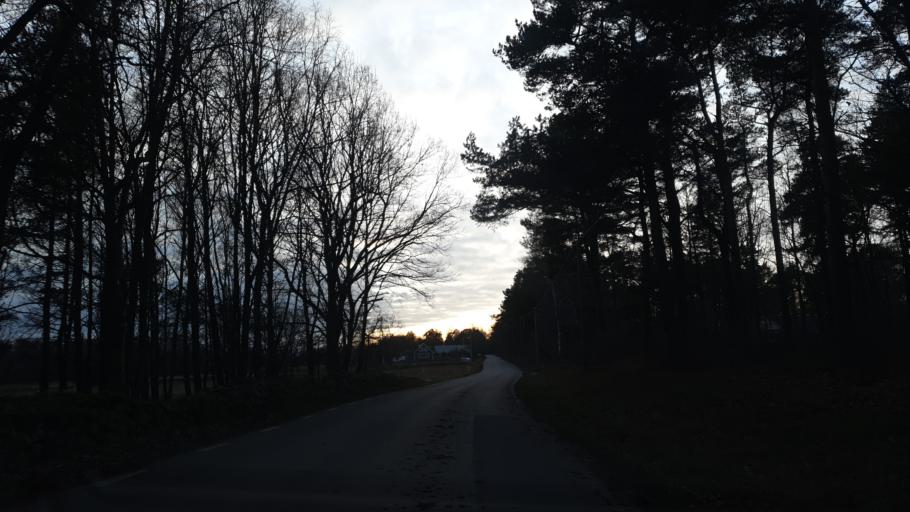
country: SE
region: Blekinge
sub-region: Karlskrona Kommun
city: Jaemjoe
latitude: 56.1629
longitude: 15.9189
